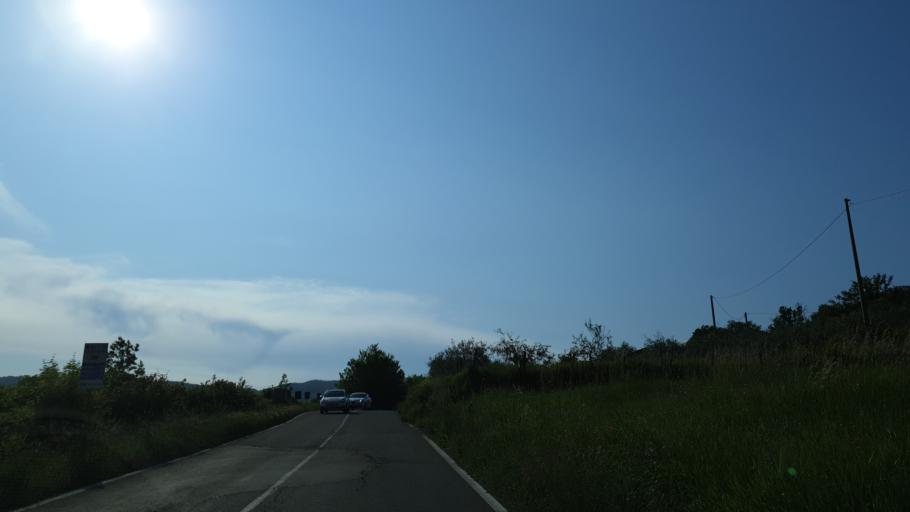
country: IT
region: Tuscany
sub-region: Province of Arezzo
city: Strada
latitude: 43.7624
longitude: 11.7085
